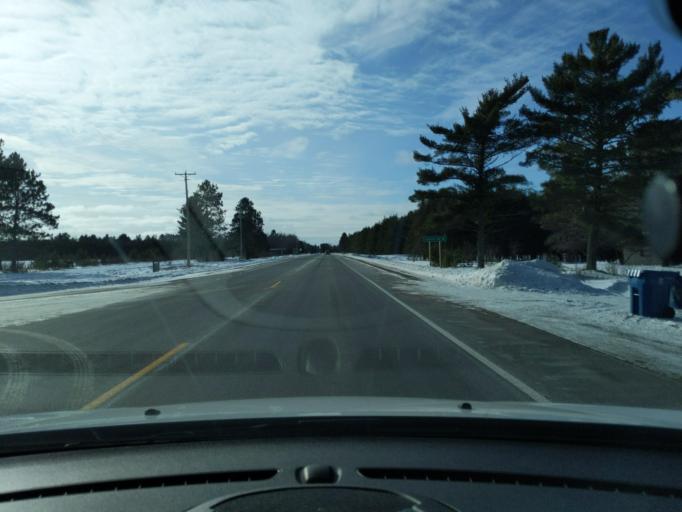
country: US
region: Wisconsin
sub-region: Sawyer County
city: Hayward
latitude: 46.0995
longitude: -91.3821
